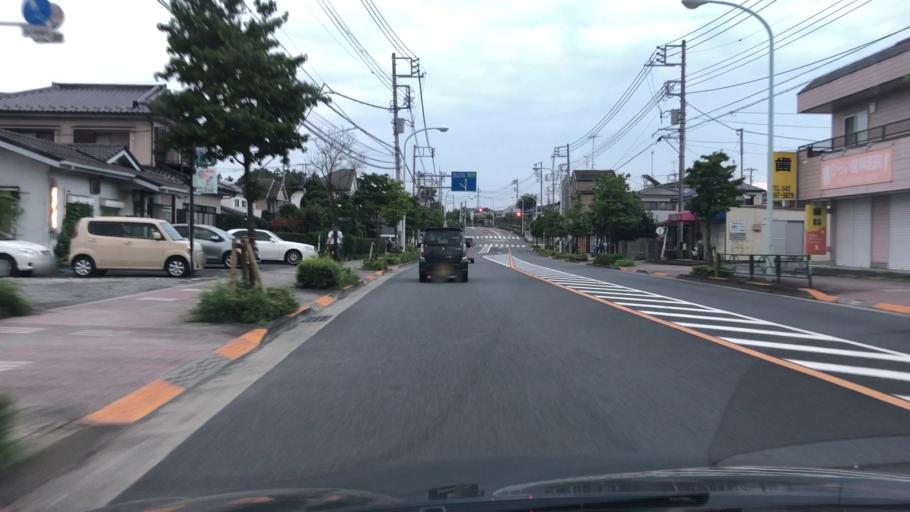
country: JP
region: Tokyo
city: Ome
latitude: 35.7401
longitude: 139.2707
